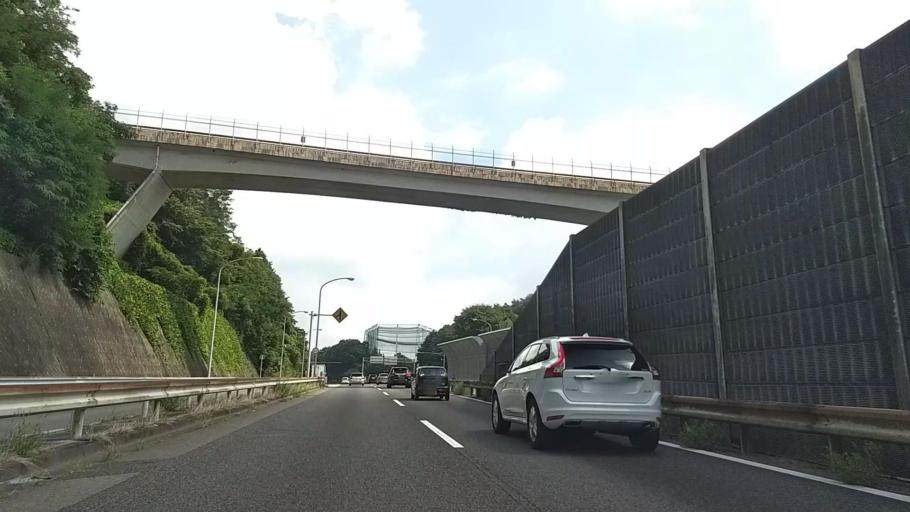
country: JP
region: Tokyo
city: Hachioji
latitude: 35.6099
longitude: 139.3396
